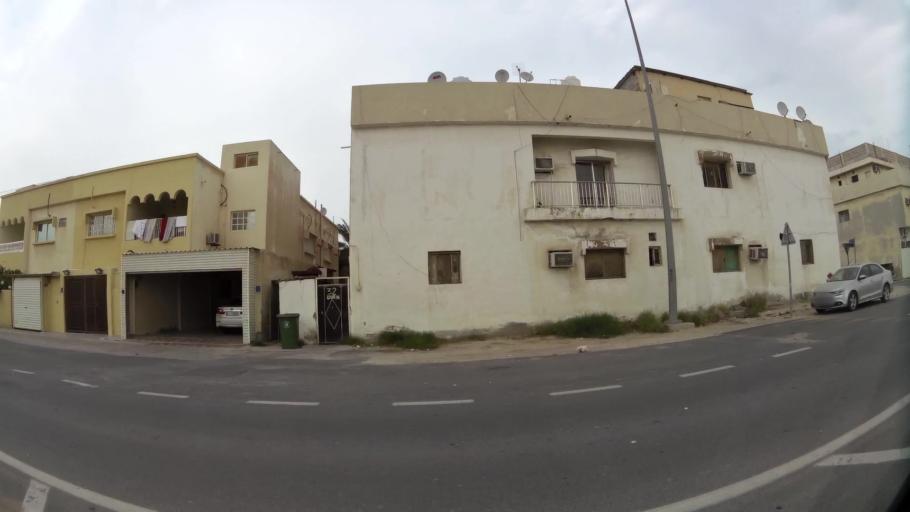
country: QA
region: Baladiyat ad Dawhah
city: Doha
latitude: 25.3185
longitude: 51.4909
